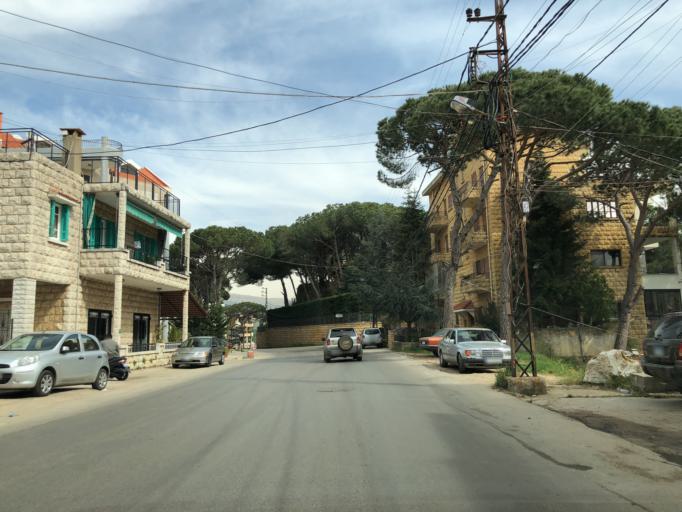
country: LB
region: Mont-Liban
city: Bhamdoun el Mhatta
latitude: 33.8892
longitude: 35.6591
